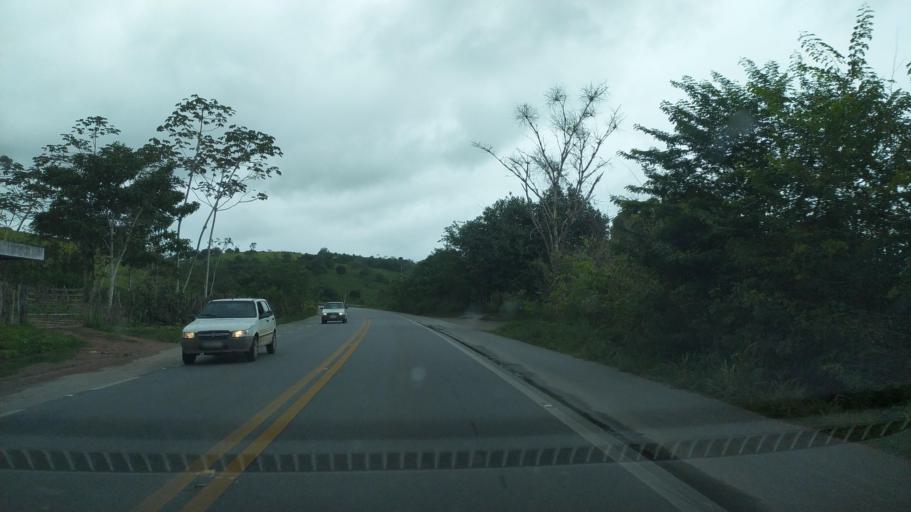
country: BR
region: Alagoas
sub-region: Uniao Dos Palmares
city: Uniao dos Palmares
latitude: -9.2181
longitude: -36.0316
